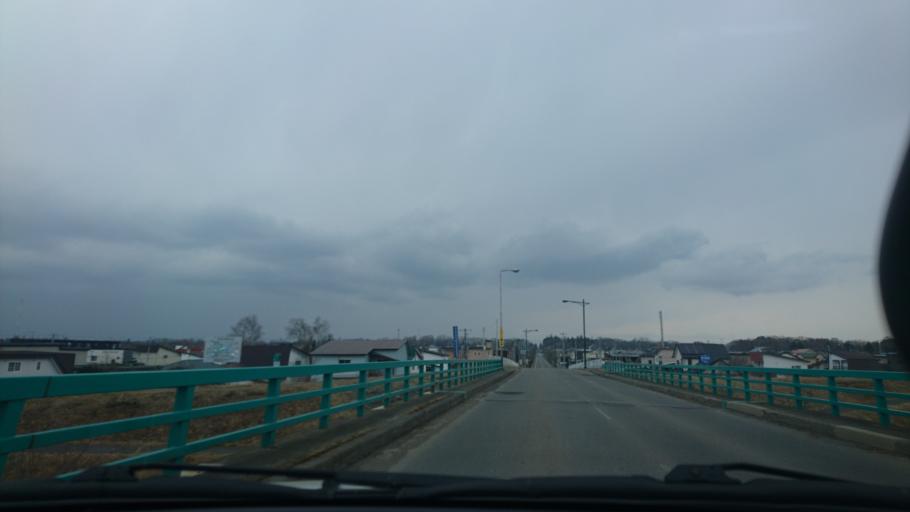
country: JP
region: Hokkaido
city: Otofuke
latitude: 42.9929
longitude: 143.2122
